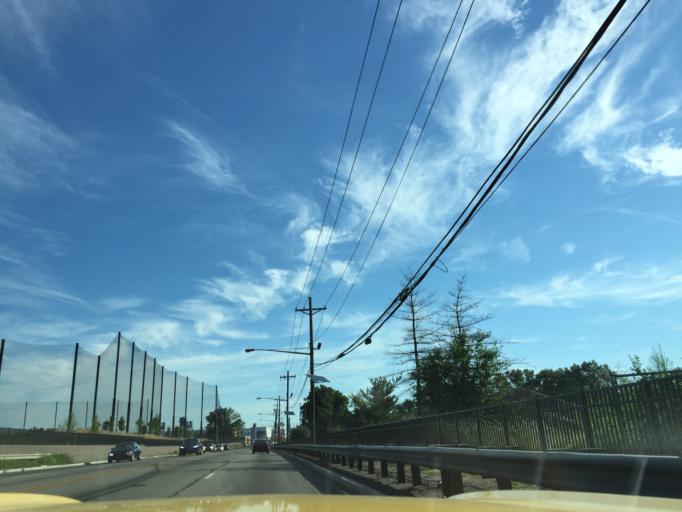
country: US
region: New Jersey
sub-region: Hudson County
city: Jersey City
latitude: 40.7275
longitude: -74.0873
